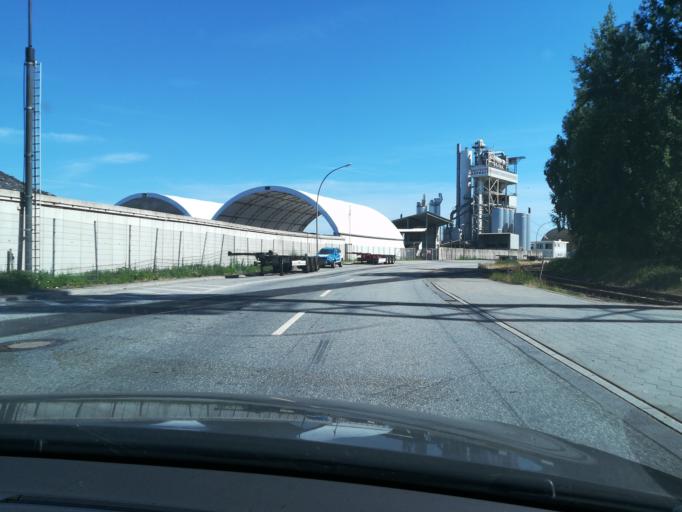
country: DE
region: Hamburg
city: Rothenburgsort
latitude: 53.5152
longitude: 10.0557
